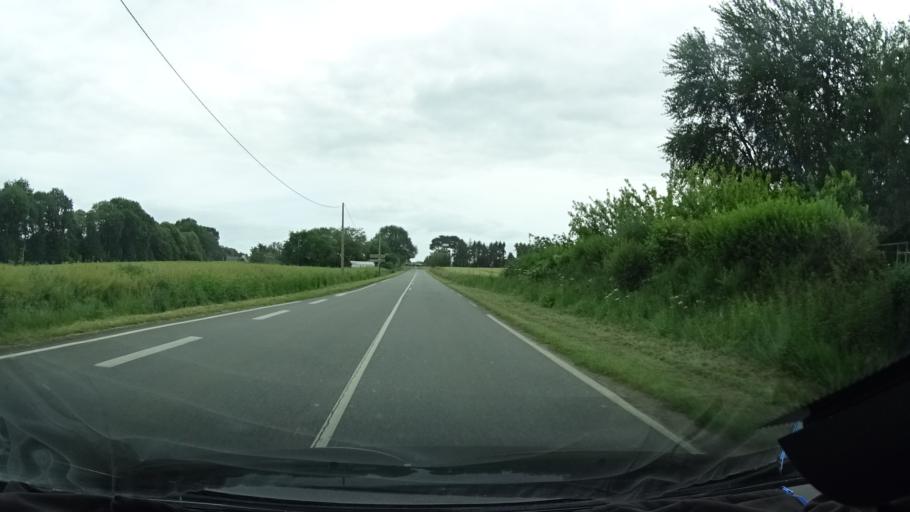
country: FR
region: Brittany
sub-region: Departement d'Ille-et-Vilaine
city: La Richardais
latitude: 48.5948
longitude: -2.0298
